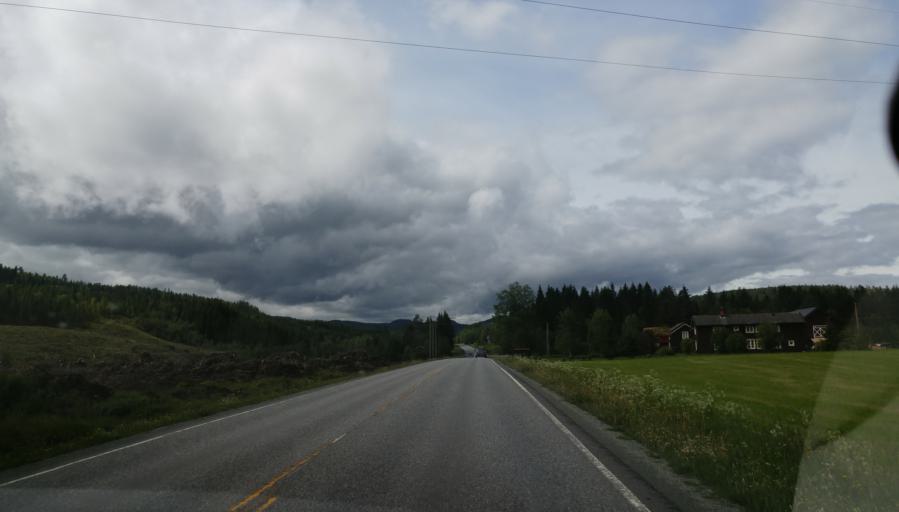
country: NO
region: Nord-Trondelag
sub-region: Stjordal
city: Stjordalshalsen
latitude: 63.3952
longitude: 11.0269
